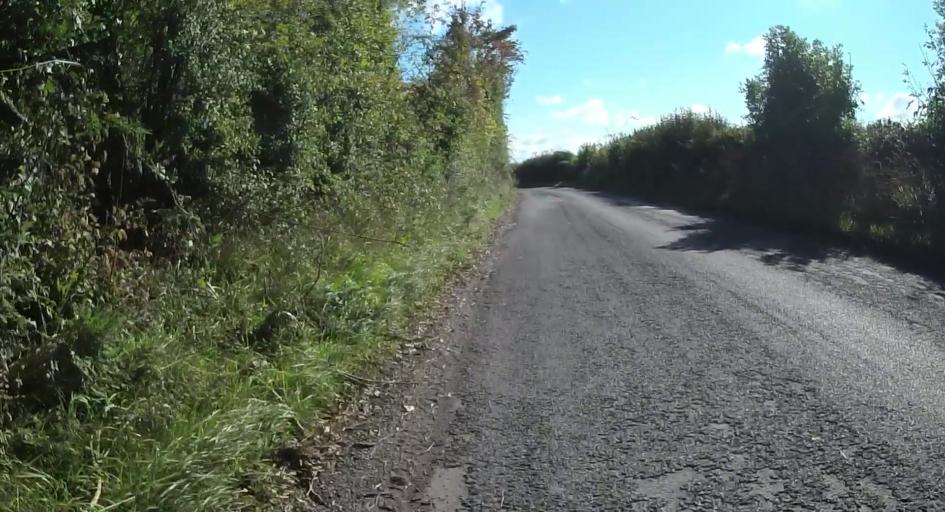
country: GB
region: England
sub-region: Hampshire
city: Hook
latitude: 51.2552
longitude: -0.9857
